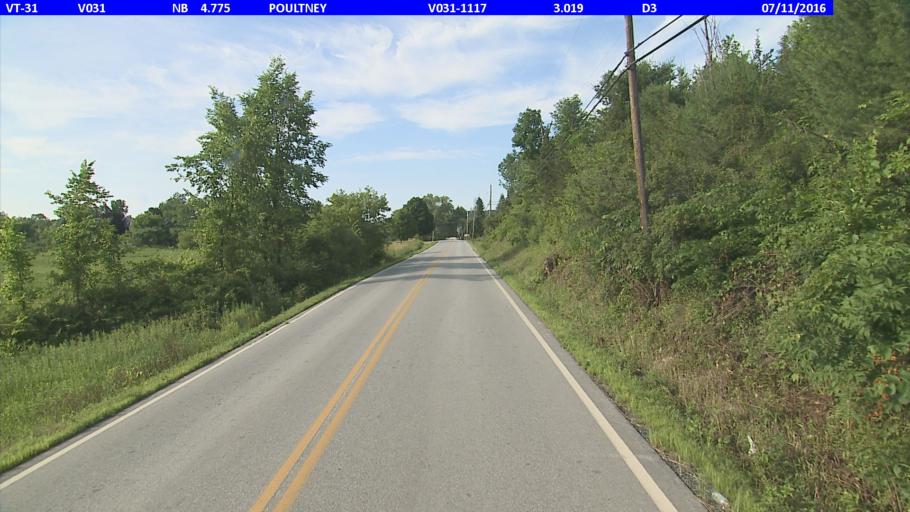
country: US
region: Vermont
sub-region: Rutland County
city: Poultney
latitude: 43.5050
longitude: -73.2356
